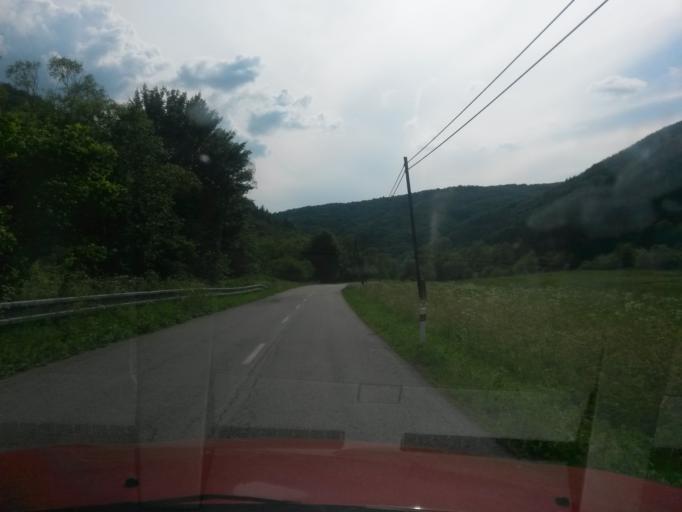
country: SK
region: Presovsky
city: Snina
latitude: 49.1217
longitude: 22.0815
